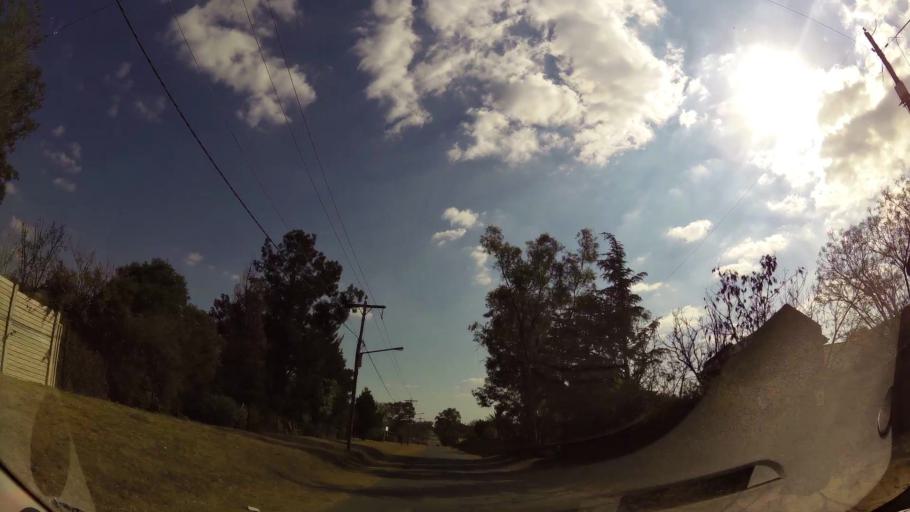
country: ZA
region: Gauteng
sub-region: Ekurhuleni Metropolitan Municipality
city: Benoni
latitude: -26.0988
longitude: 28.3509
